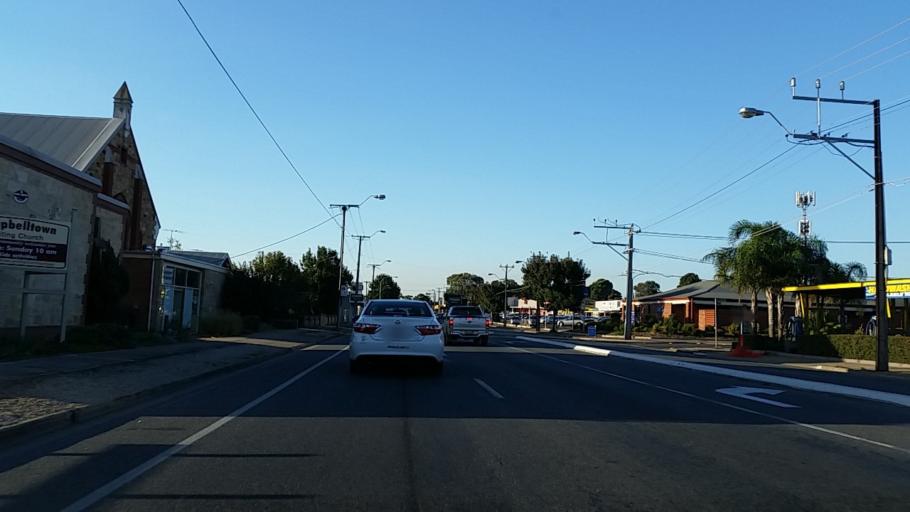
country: AU
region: South Australia
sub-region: Campbelltown
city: Campbelltown
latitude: -34.8798
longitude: 138.6626
